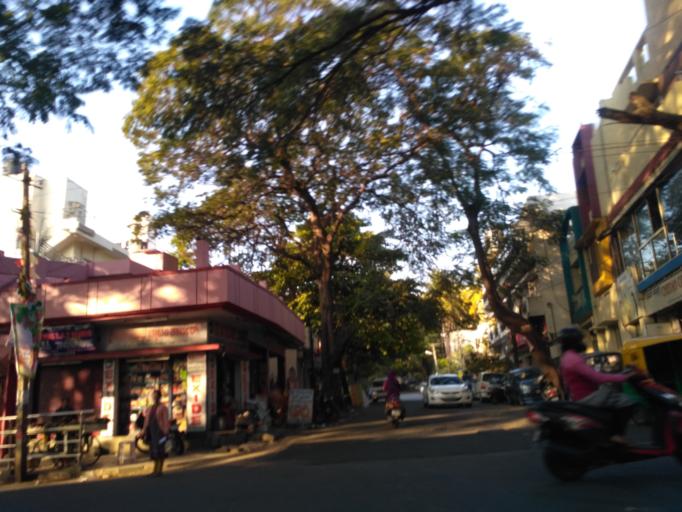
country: IN
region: Karnataka
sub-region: Bangalore Urban
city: Bangalore
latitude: 12.9651
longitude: 77.5382
